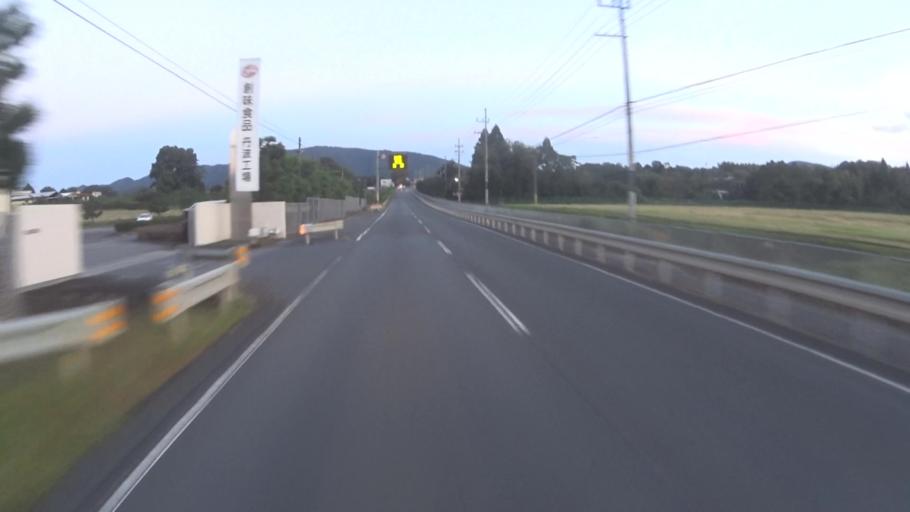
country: JP
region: Kyoto
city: Ayabe
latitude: 35.1777
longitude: 135.4221
